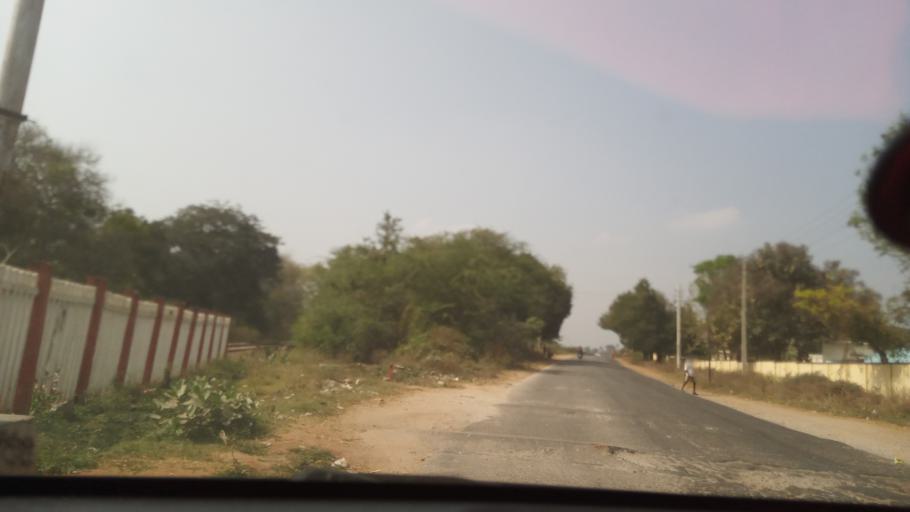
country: IN
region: Karnataka
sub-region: Mysore
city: Nanjangud
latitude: 12.0846
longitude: 76.7315
